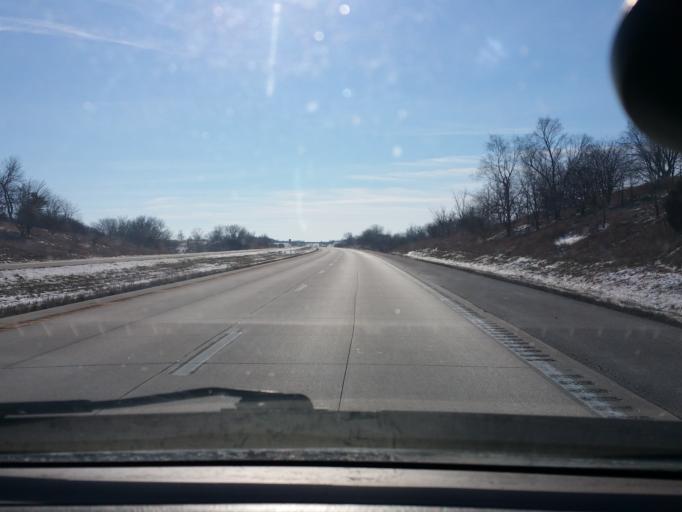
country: US
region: Missouri
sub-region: Daviess County
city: Gallatin
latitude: 40.0082
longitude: -94.0967
